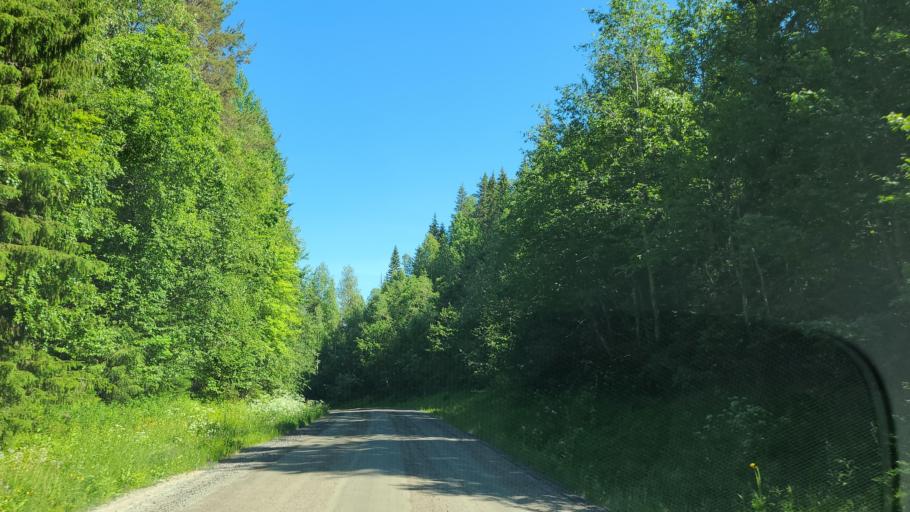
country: SE
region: Vaesterbotten
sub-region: Nordmalings Kommun
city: Nordmaling
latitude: 63.6464
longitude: 19.2347
